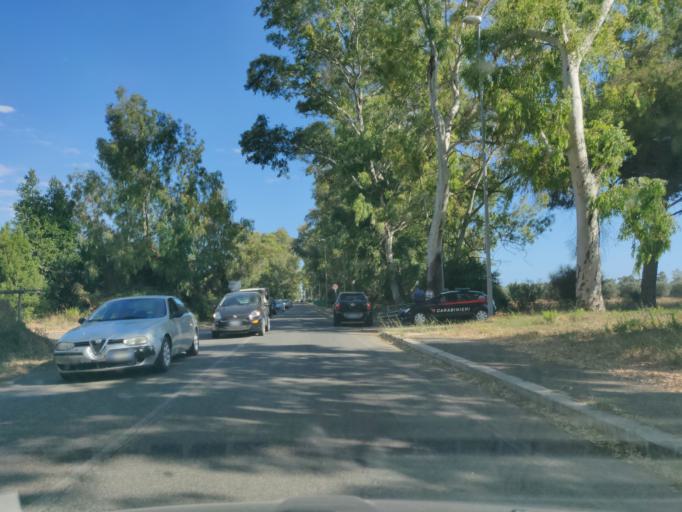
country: IT
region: Latium
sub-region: Citta metropolitana di Roma Capitale
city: Aurelia
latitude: 42.1454
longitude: 11.7627
